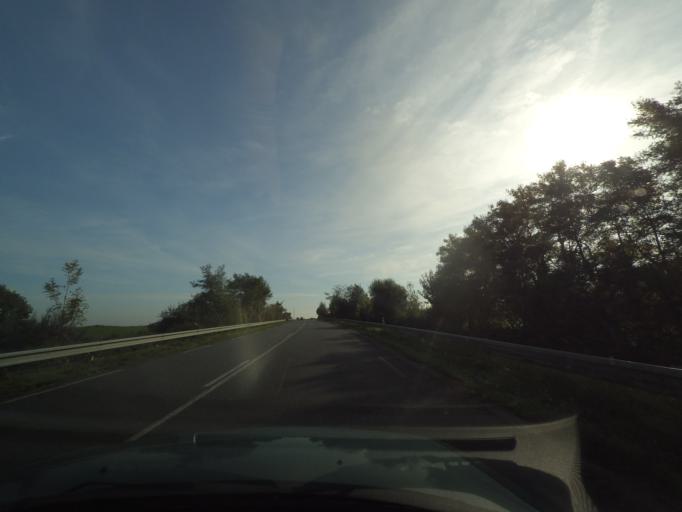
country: FR
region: Pays de la Loire
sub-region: Departement de Maine-et-Loire
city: La Romagne
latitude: 47.0585
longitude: -1.0025
